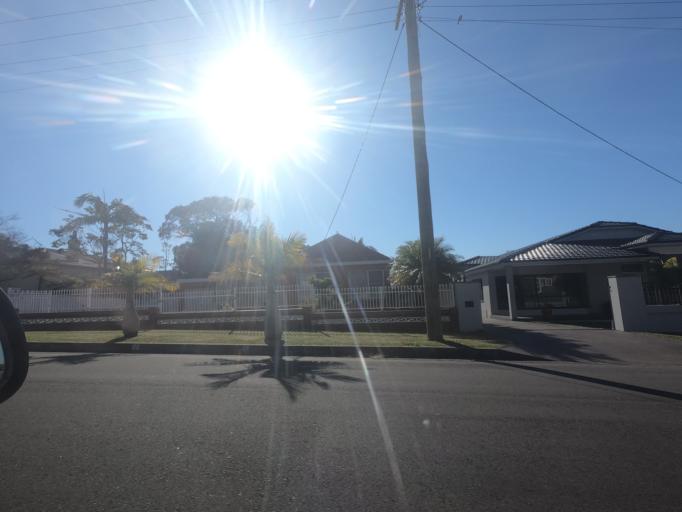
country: AU
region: New South Wales
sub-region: Wollongong
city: Corrimal
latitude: -34.3840
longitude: 150.8924
